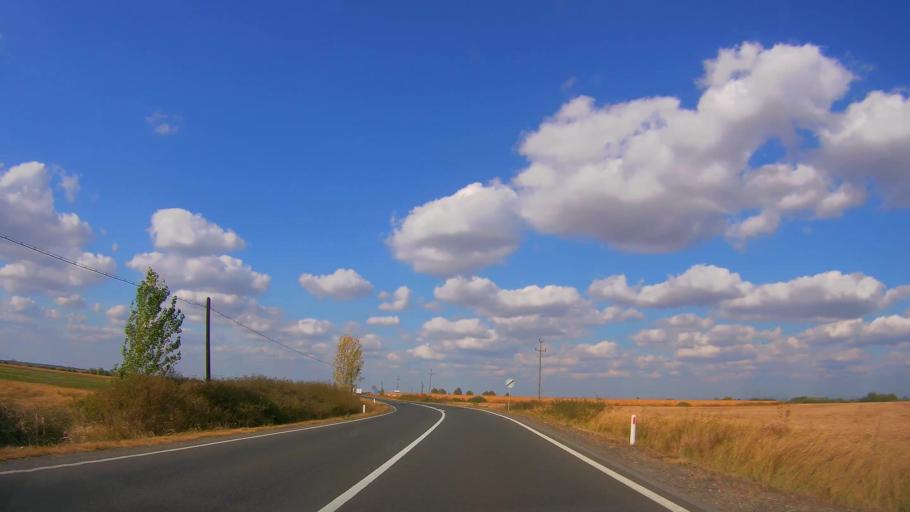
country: RO
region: Satu Mare
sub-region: Oras Ardud
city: Madaras
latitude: 47.7047
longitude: 22.8724
